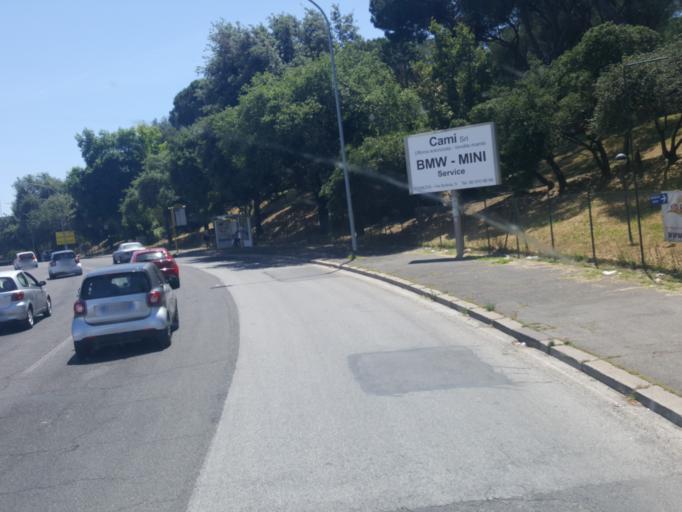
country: IT
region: Latium
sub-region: Citta metropolitana di Roma Capitale
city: Selcetta
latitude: 41.8245
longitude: 12.4643
